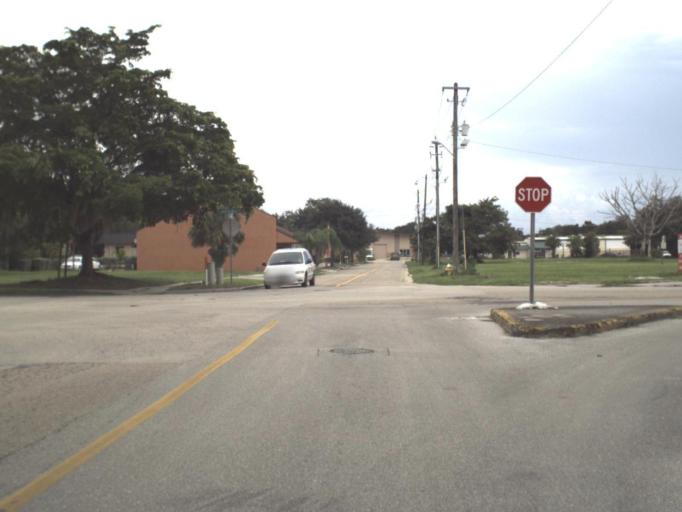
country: US
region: Florida
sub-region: Lee County
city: Fort Myers
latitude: 26.6385
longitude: -81.8669
